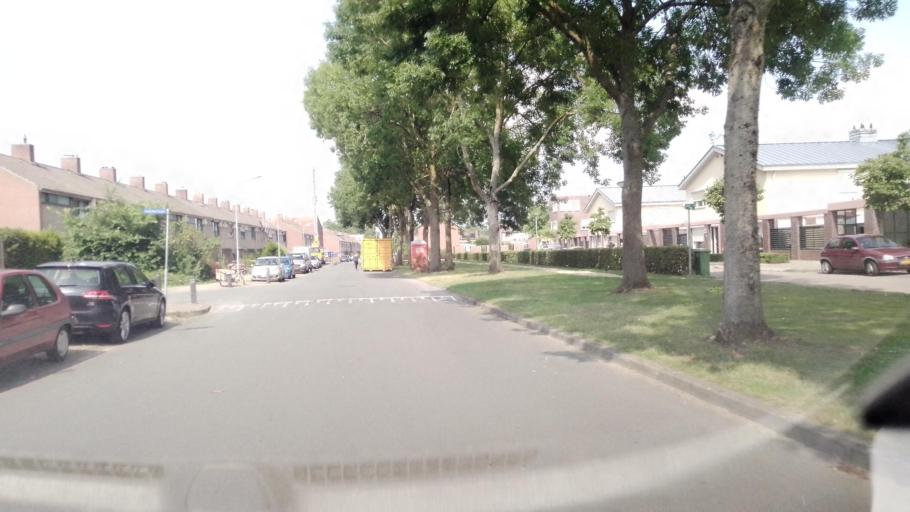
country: NL
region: Limburg
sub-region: Gemeente Venlo
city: Venlo
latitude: 51.3594
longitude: 6.1700
